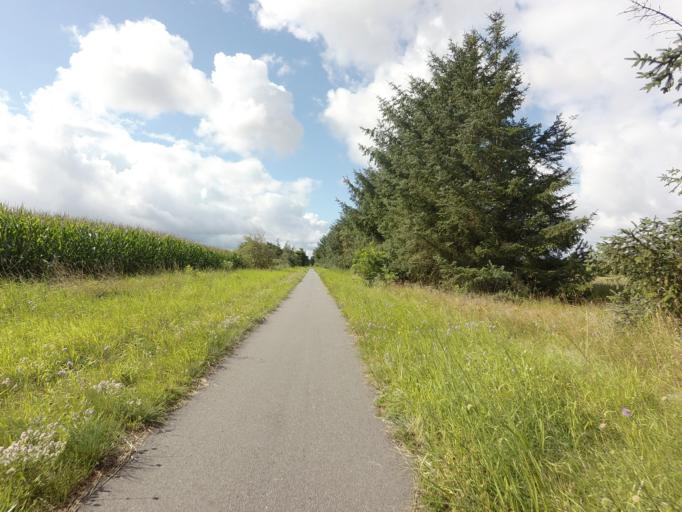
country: DK
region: Central Jutland
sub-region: Silkeborg Kommune
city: Svejbaek
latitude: 56.2084
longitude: 9.6719
